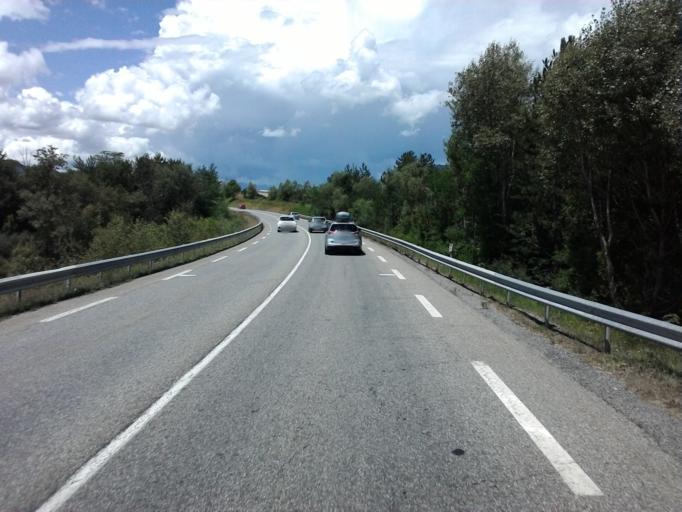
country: FR
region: Provence-Alpes-Cote d'Azur
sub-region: Departement des Hautes-Alpes
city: Chorges
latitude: 44.5374
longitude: 6.2977
